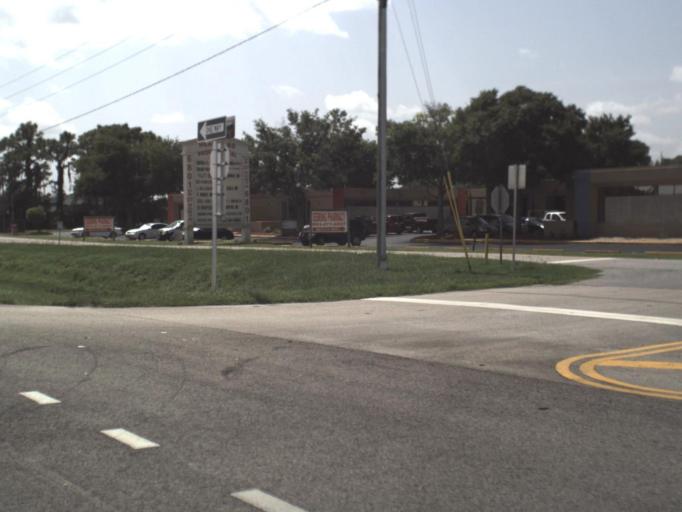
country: US
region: Florida
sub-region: Highlands County
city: Avon Park
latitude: 27.5442
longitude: -81.5060
